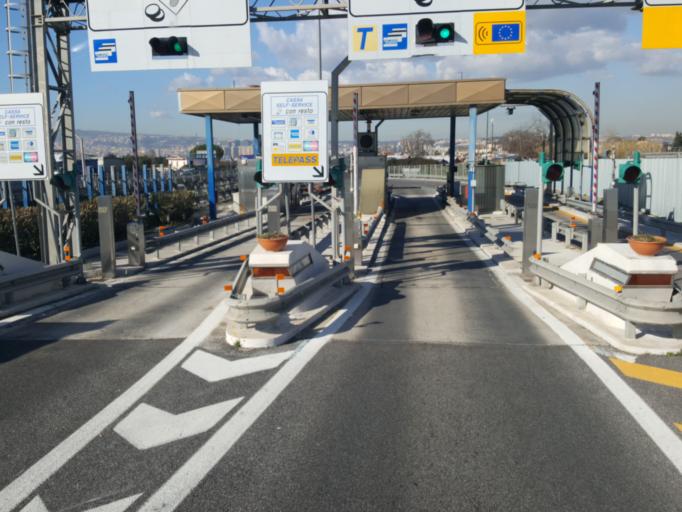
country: IT
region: Campania
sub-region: Provincia di Napoli
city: San Giorgio a Cremano
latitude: 40.8420
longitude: 14.3288
